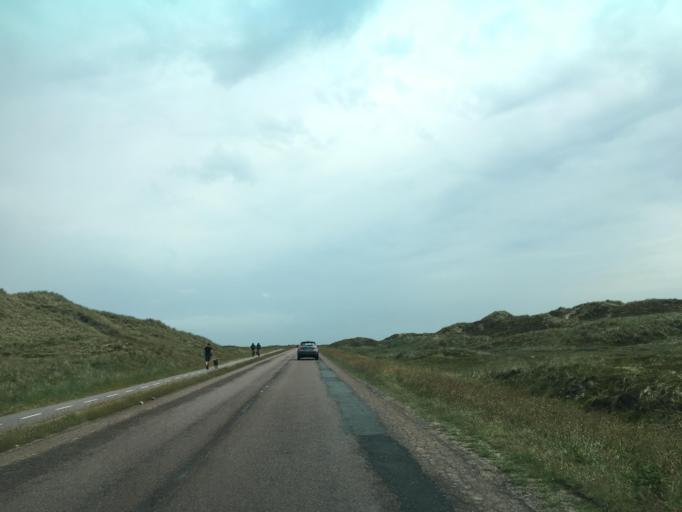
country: DK
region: North Denmark
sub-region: Thisted Kommune
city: Hurup
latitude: 56.9583
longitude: 8.3794
